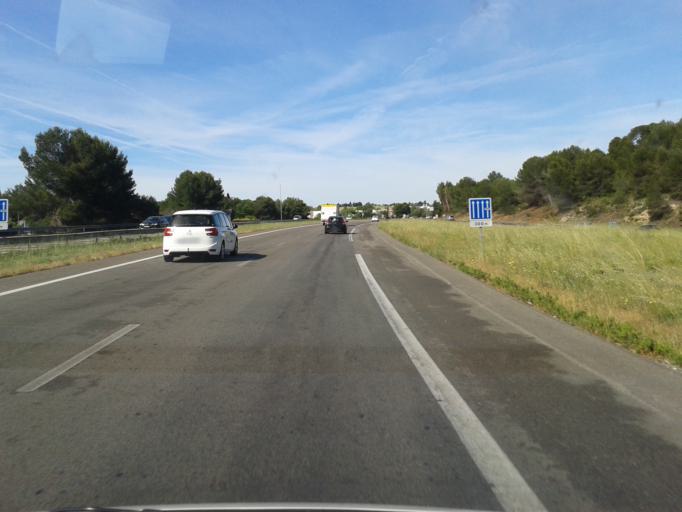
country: FR
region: Provence-Alpes-Cote d'Azur
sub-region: Departement des Bouches-du-Rhone
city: Cabries
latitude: 43.4303
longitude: 5.3914
